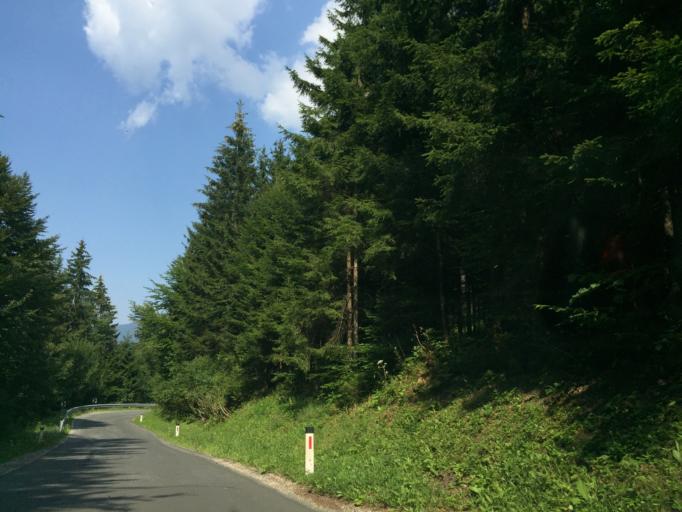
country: SI
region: Slovenj Gradec
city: Smartno pri Slovenj Gradcu
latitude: 46.4399
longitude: 15.1145
